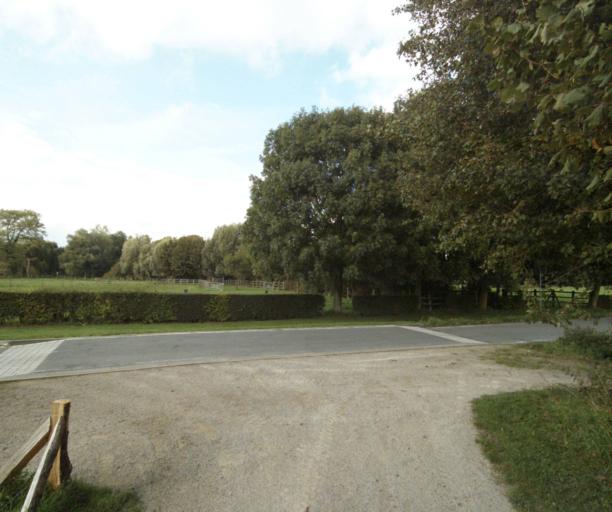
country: FR
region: Nord-Pas-de-Calais
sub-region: Departement du Nord
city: Wavrin
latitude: 50.5646
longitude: 2.9406
